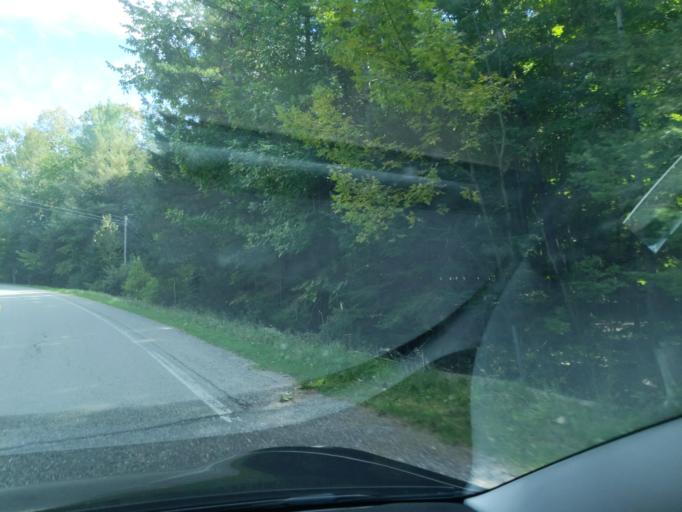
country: US
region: Michigan
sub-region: Antrim County
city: Bellaire
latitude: 45.0502
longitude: -85.3147
